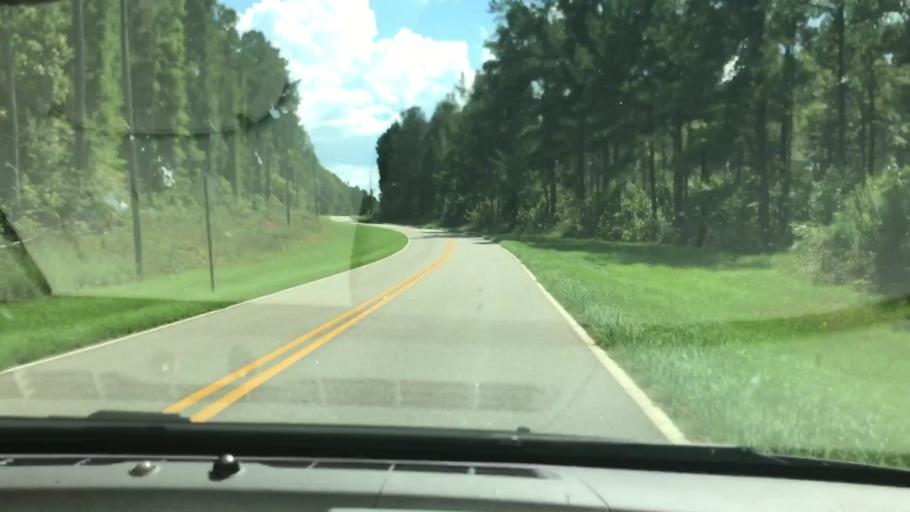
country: US
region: Georgia
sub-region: Troup County
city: La Grange
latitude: 33.1442
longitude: -85.1154
